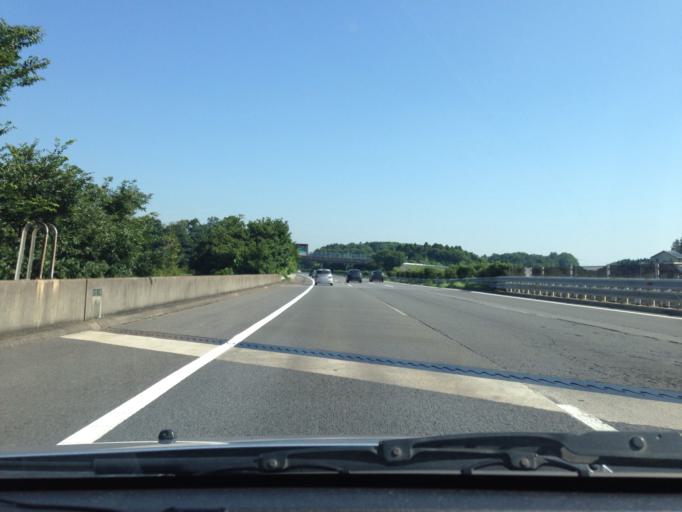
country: JP
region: Ibaraki
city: Naka
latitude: 36.0649
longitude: 140.1577
